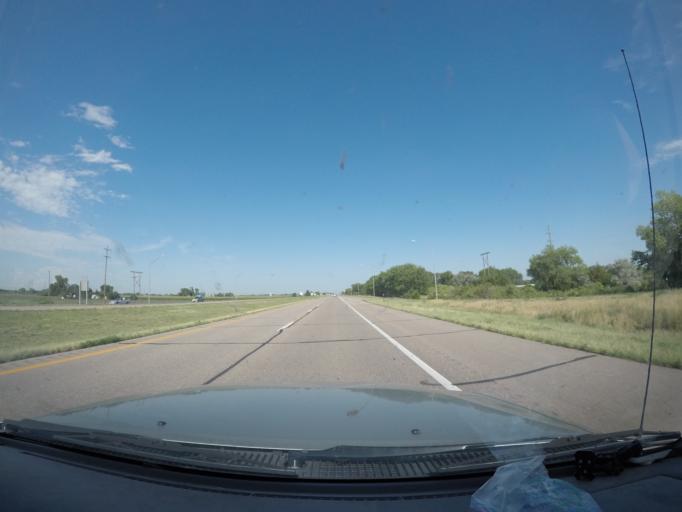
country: US
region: Nebraska
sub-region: Phelps County
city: Holdrege
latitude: 40.6900
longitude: -99.3767
